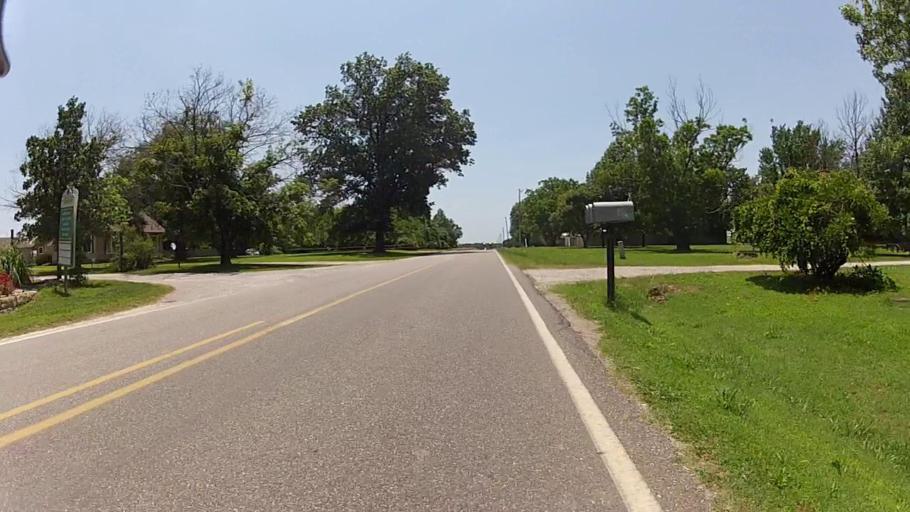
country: US
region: Kansas
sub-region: Montgomery County
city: Cherryvale
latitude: 37.2583
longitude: -95.5370
